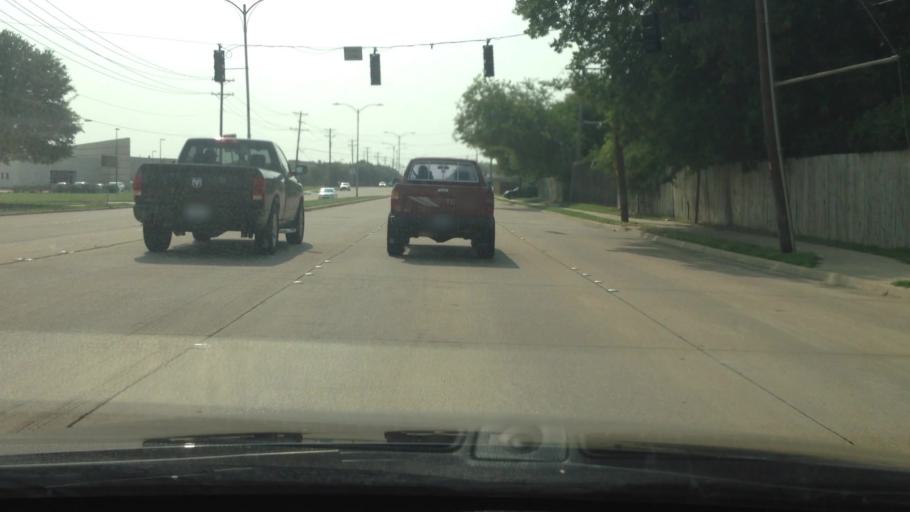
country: US
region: Texas
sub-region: Tarrant County
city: Watauga
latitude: 32.8604
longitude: -97.2303
